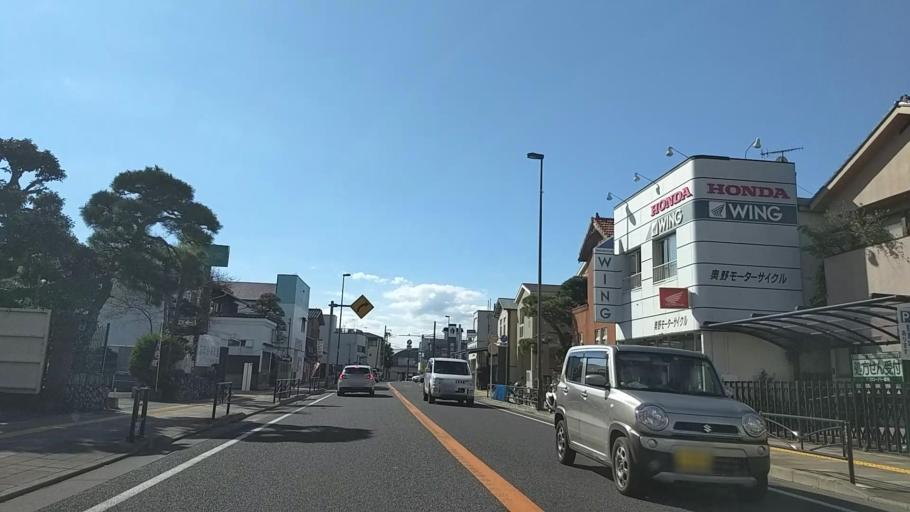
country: JP
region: Kanagawa
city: Oiso
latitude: 35.3083
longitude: 139.3148
